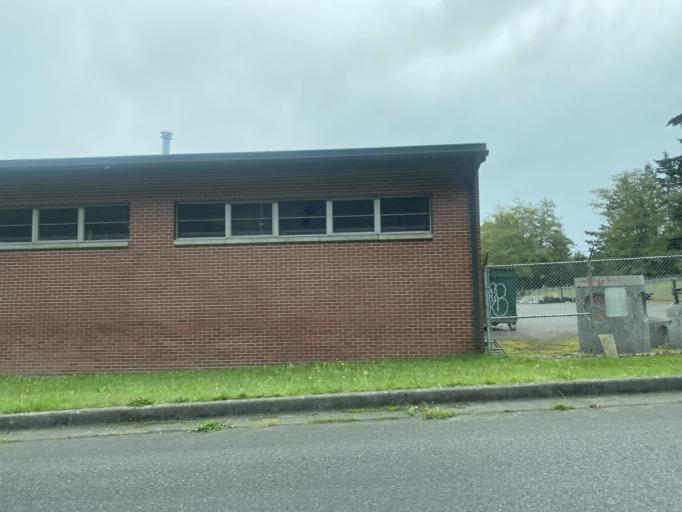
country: US
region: Washington
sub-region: King County
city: Seattle
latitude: 47.6612
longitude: -122.4056
